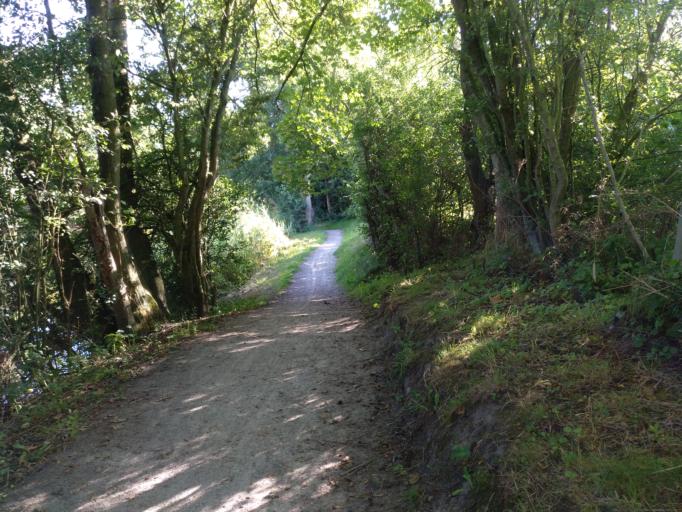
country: DE
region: Lower Saxony
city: Otterndorf
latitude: 53.8204
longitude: 8.8856
